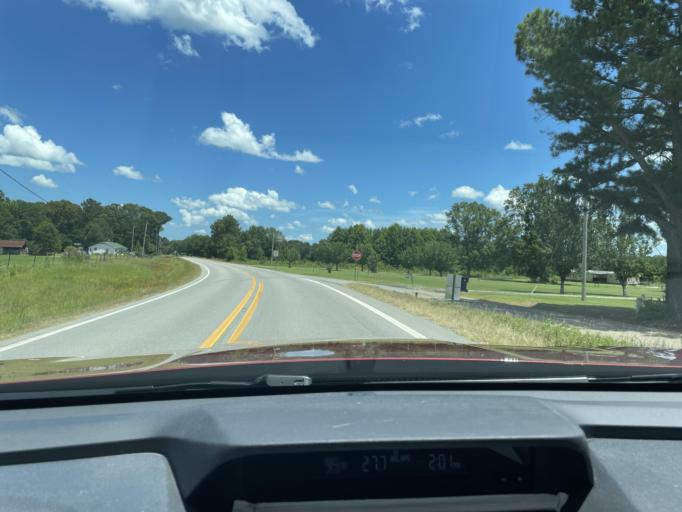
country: US
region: Arkansas
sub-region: Drew County
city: Monticello
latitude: 33.6049
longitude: -91.7336
